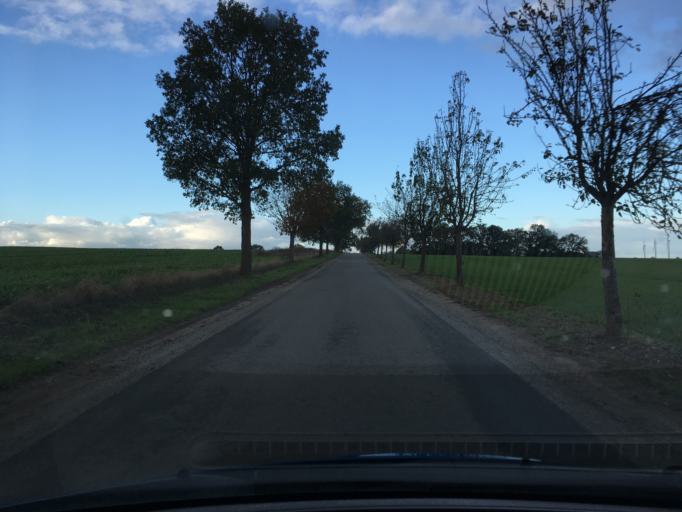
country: DE
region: Lower Saxony
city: Reinstorf
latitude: 53.2379
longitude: 10.5677
